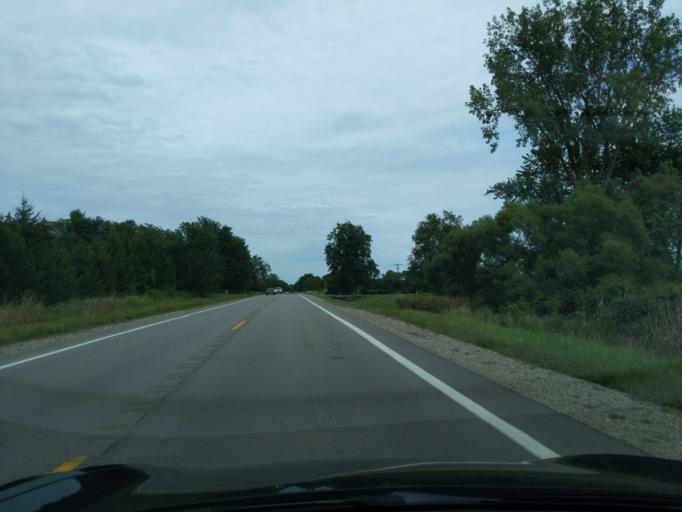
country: US
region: Michigan
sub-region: Barry County
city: Nashville
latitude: 42.5673
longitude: -85.0307
